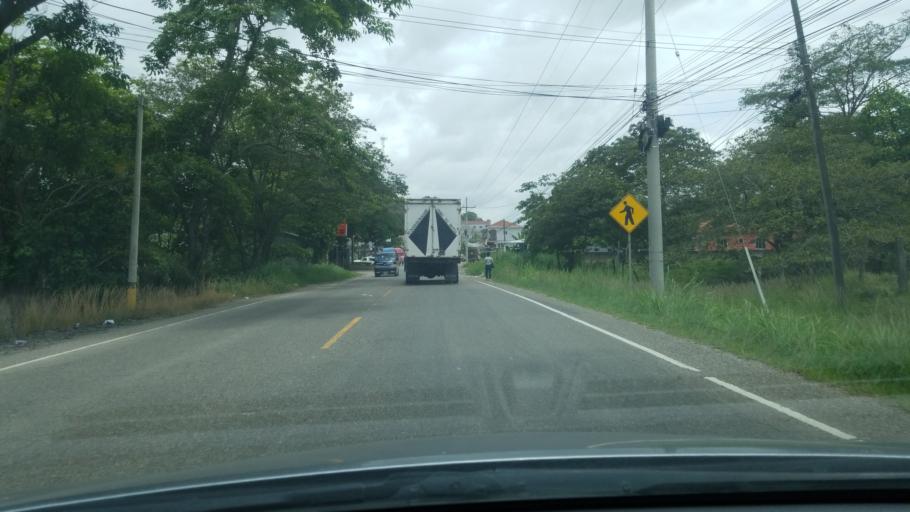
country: HN
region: Copan
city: Cucuyagua
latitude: 14.6616
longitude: -88.8717
